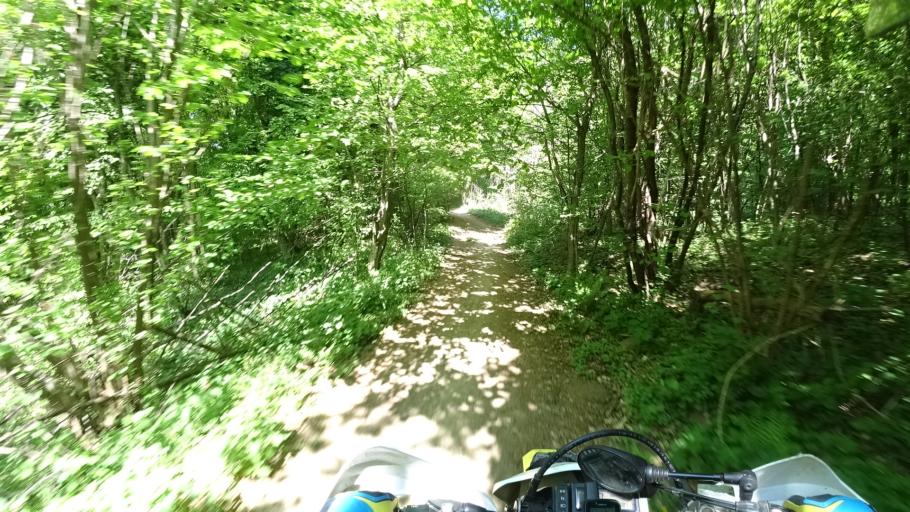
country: HR
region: Zagrebacka
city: Jablanovec
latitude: 45.8521
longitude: 15.8578
